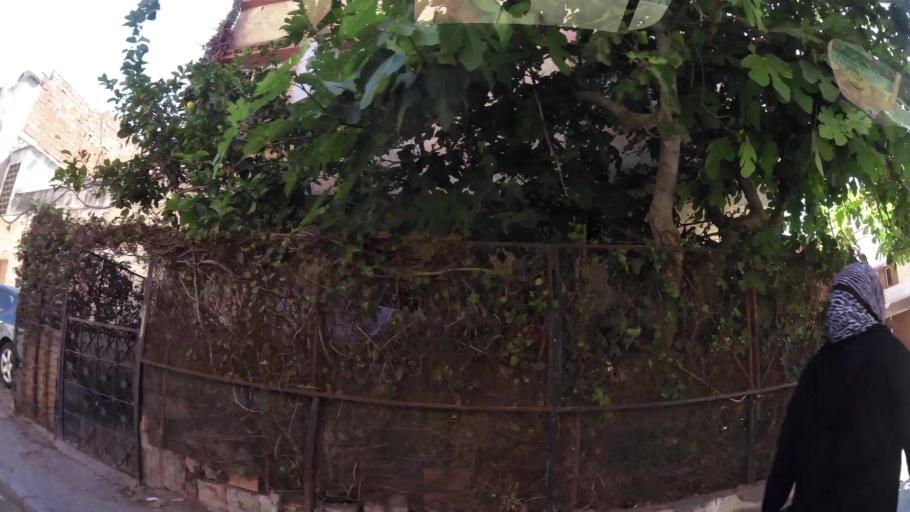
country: MA
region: Gharb-Chrarda-Beni Hssen
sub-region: Kenitra Province
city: Kenitra
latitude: 34.2415
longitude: -6.5533
